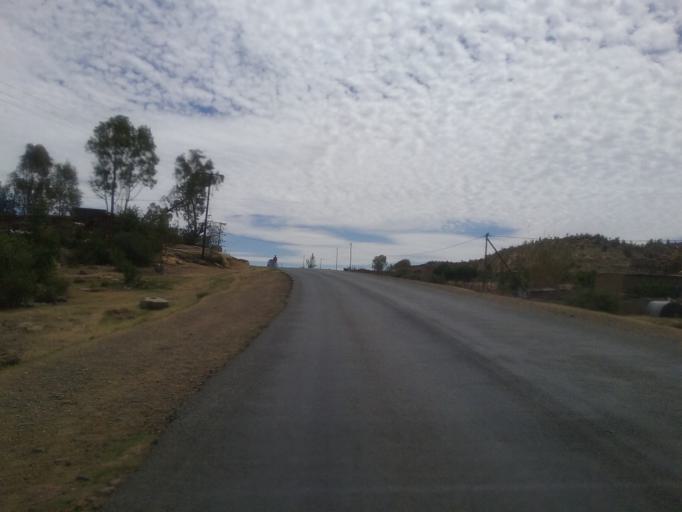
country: LS
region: Mafeteng
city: Mafeteng
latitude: -29.8387
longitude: 27.2328
